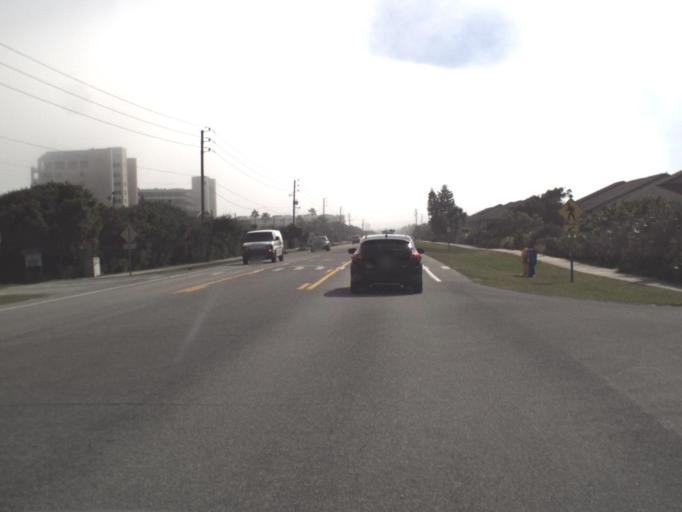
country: US
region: Florida
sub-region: Volusia County
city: Edgewater
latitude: 28.9965
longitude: -80.8715
